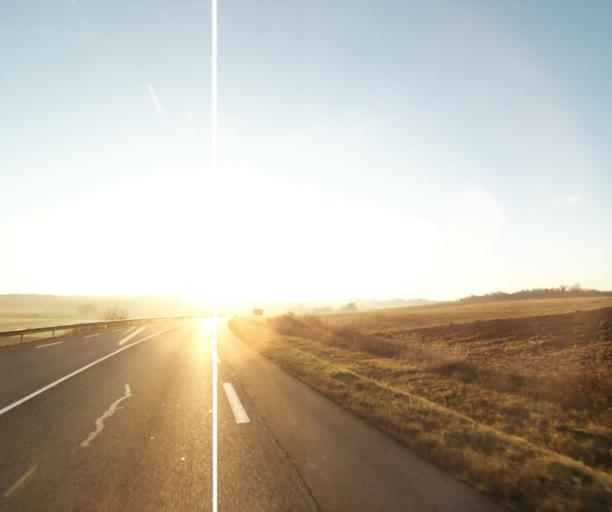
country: FR
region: Poitou-Charentes
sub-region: Departement de la Charente-Maritime
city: Chaniers
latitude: 45.7242
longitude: -0.4992
